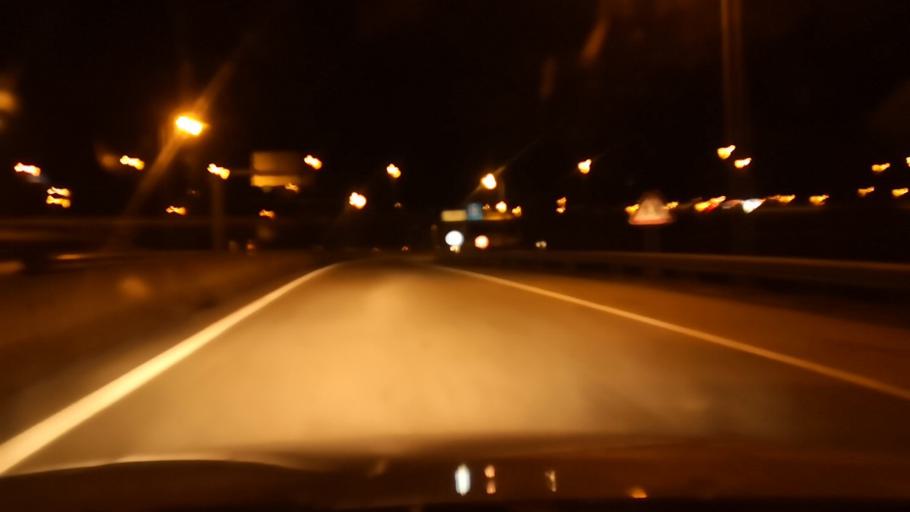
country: PT
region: Guarda
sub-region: Guarda
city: Sequeira
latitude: 40.5654
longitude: -7.2194
